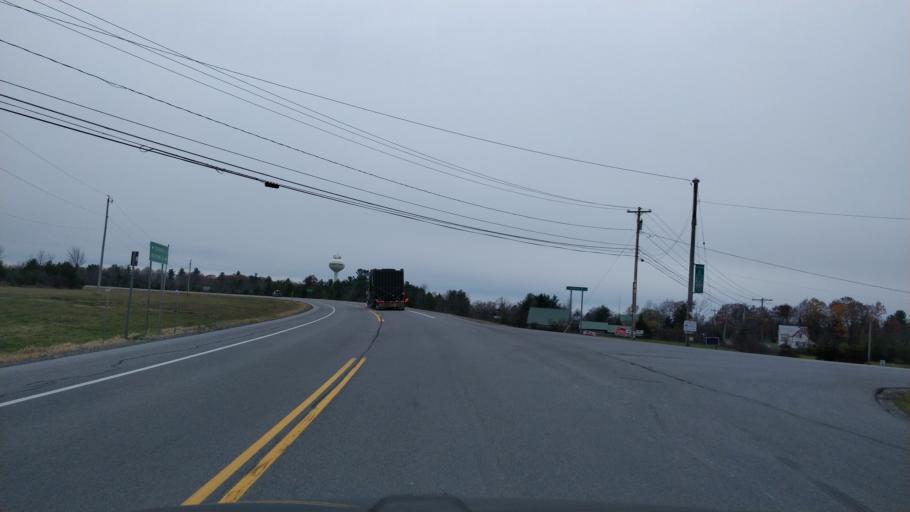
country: CA
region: Ontario
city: Brockville
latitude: 44.5929
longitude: -75.6384
